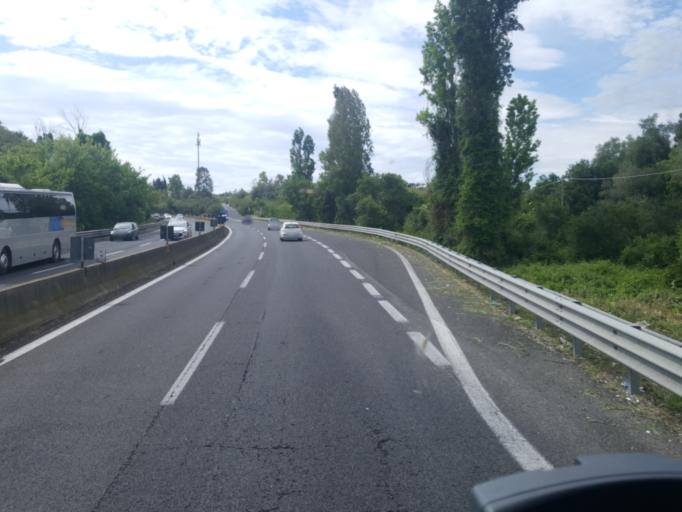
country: IT
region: Latium
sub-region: Citta metropolitana di Roma Capitale
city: Valle Santa
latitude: 41.8944
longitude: 12.2919
